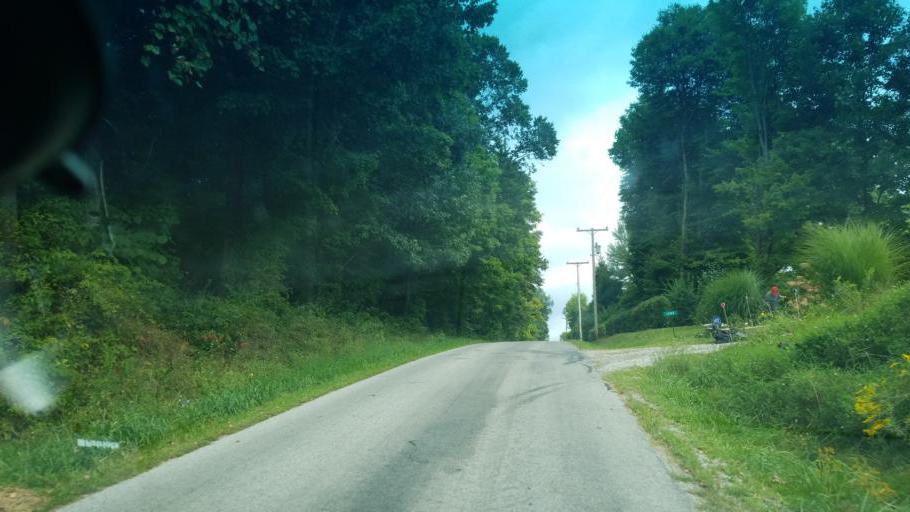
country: US
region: Ohio
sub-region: Knox County
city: Centerburg
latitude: 40.2419
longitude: -82.6643
